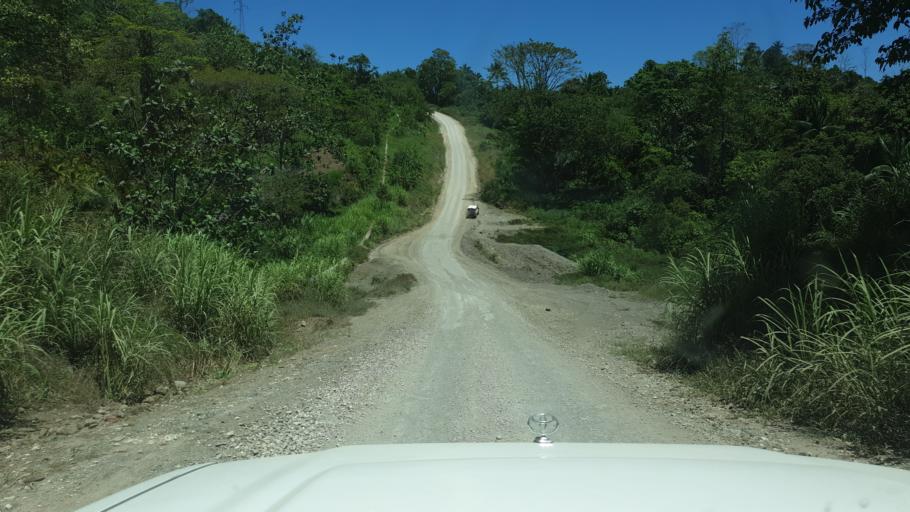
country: PG
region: Madang
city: Madang
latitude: -5.5143
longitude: 145.4313
